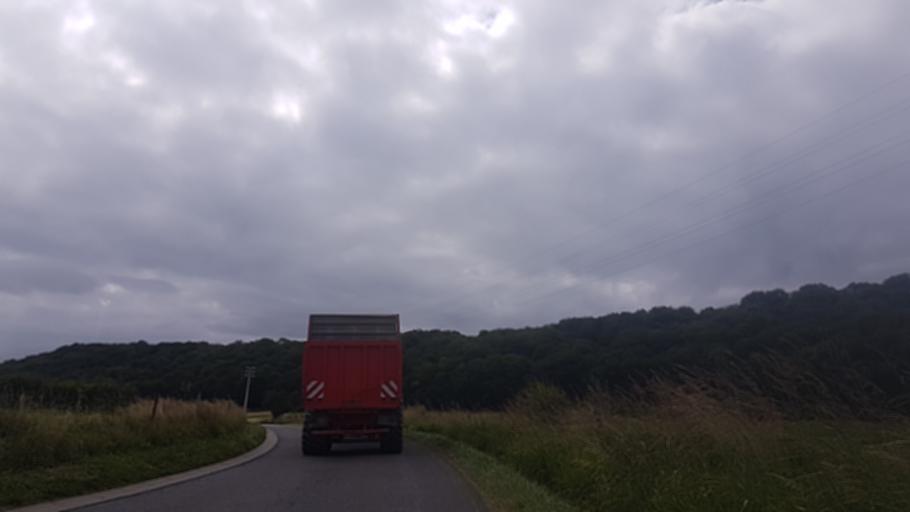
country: BE
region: Wallonia
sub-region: Province de Namur
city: Couvin
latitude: 50.1041
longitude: 4.5522
